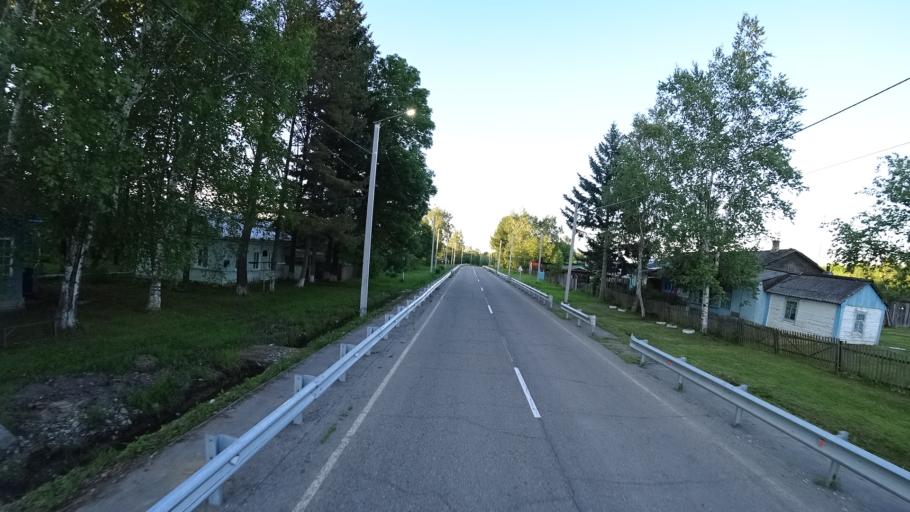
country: RU
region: Khabarovsk Krai
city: Khor
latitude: 47.8554
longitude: 134.9861
